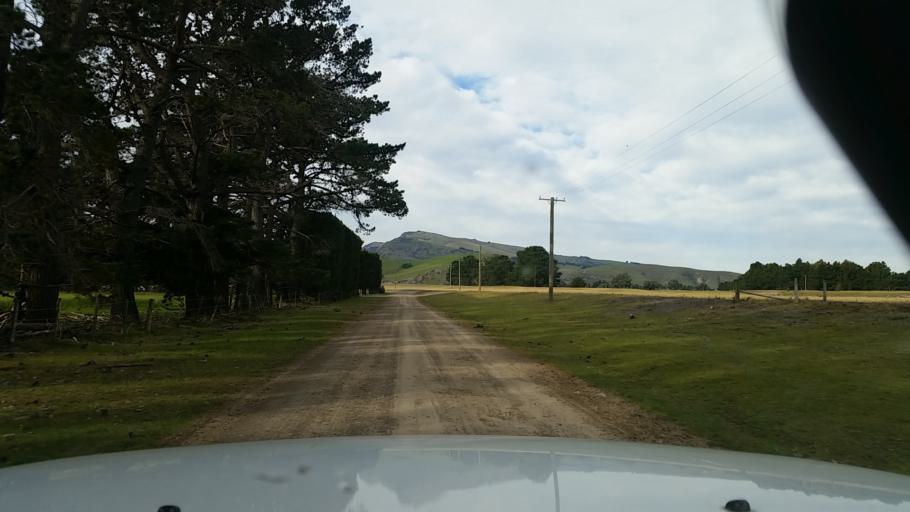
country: NZ
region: Canterbury
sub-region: Selwyn District
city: Lincoln
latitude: -43.8108
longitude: 172.6752
